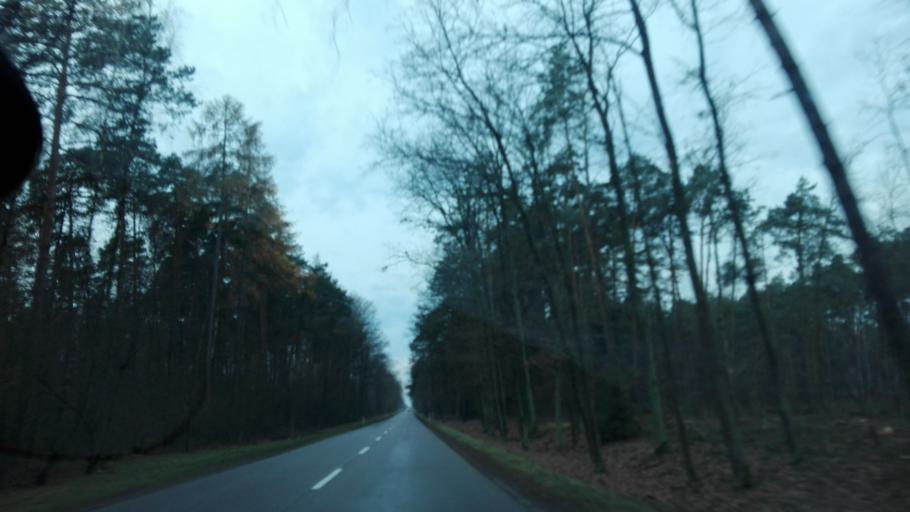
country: PL
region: Lublin Voivodeship
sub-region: Powiat radzynski
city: Radzyn Podlaski
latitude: 51.7775
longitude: 22.6726
